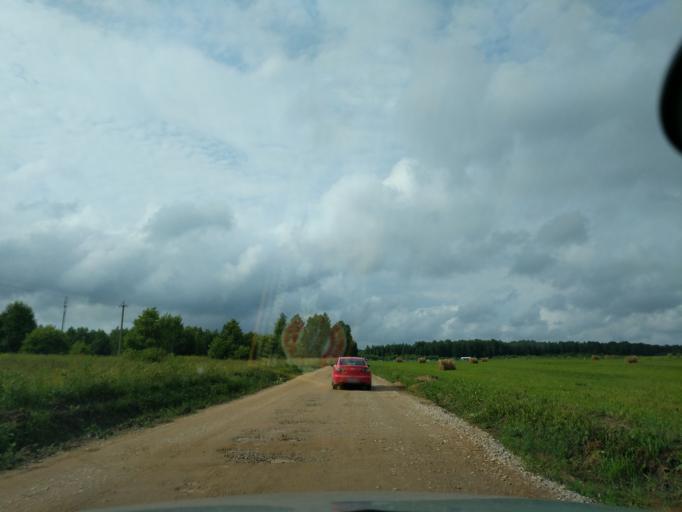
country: RU
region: Kaluga
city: Nikola-Lenivets
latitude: 54.7580
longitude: 35.6004
